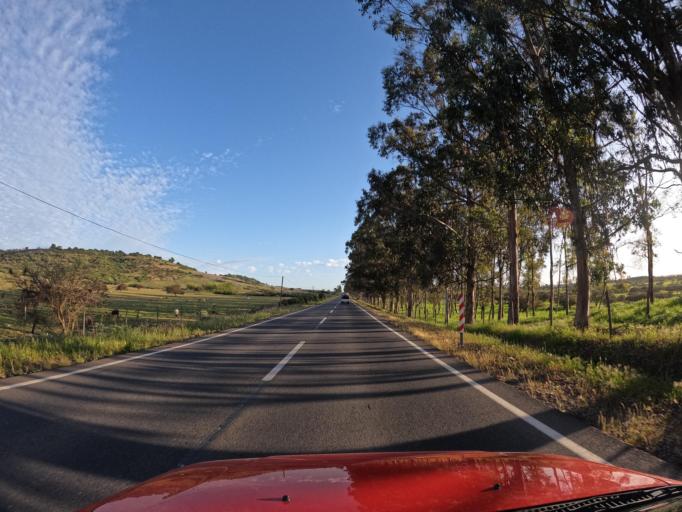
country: CL
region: O'Higgins
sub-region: Provincia de Colchagua
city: Santa Cruz
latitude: -34.1844
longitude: -71.7334
